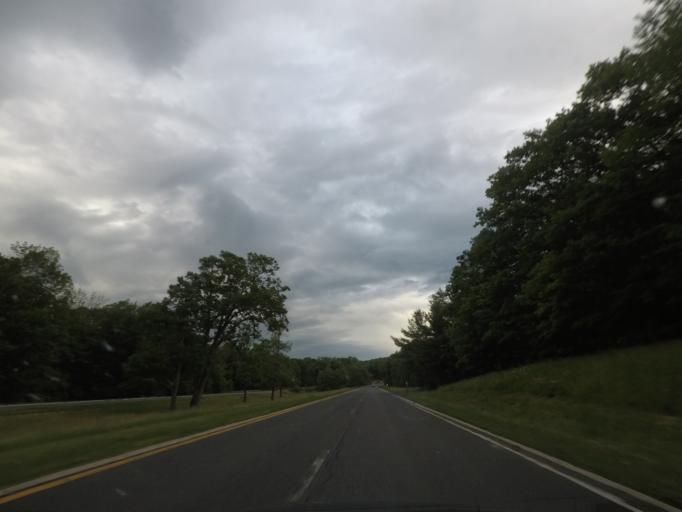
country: US
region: New York
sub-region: Columbia County
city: Philmont
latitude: 42.1765
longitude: -73.6629
